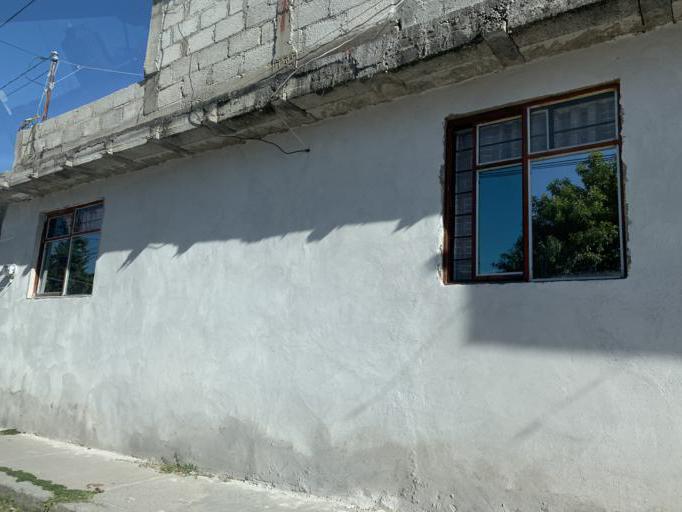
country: MX
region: Puebla
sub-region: Puebla
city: El Capulo (La Quebradora)
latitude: 18.9534
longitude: -98.2483
